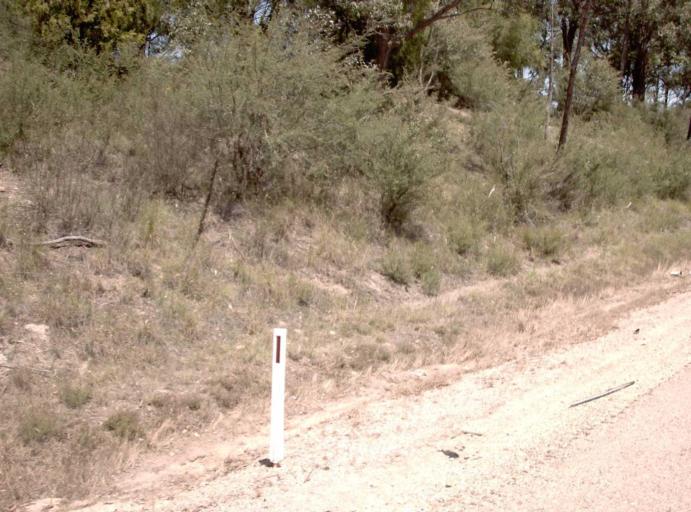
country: AU
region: Victoria
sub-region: East Gippsland
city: Bairnsdale
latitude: -37.7294
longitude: 147.7890
